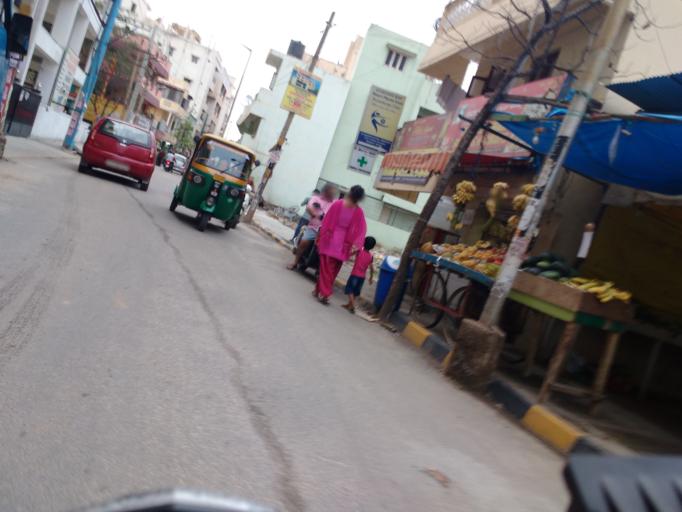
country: IN
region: Karnataka
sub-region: Bangalore Urban
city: Bangalore
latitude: 12.9927
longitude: 77.6677
